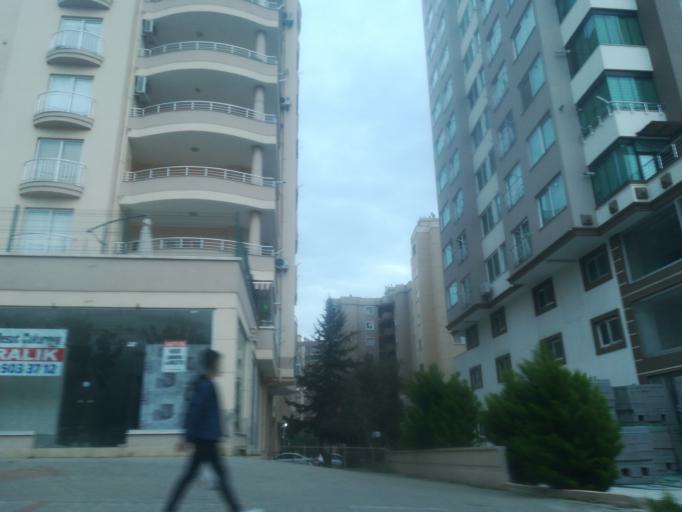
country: TR
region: Adana
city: Adana
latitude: 37.0436
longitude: 35.2913
